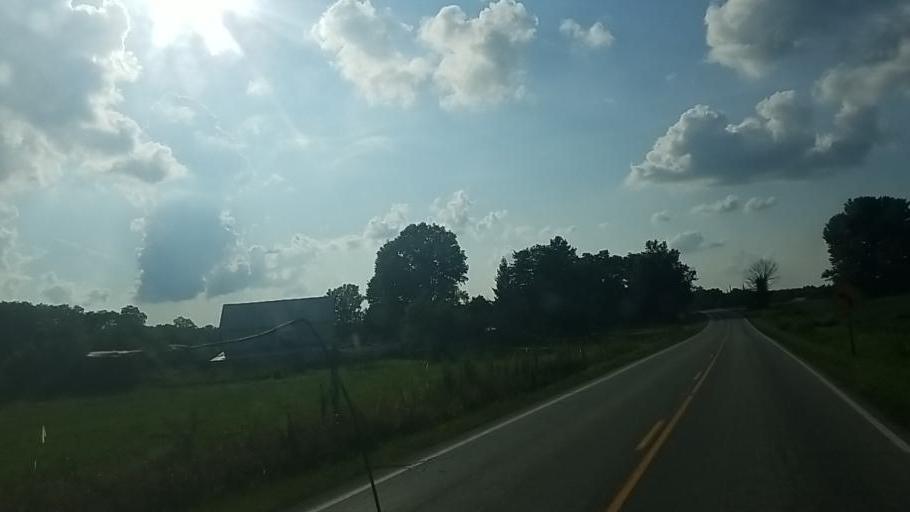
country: US
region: Ohio
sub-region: Wayne County
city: West Salem
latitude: 40.8816
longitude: -82.1135
